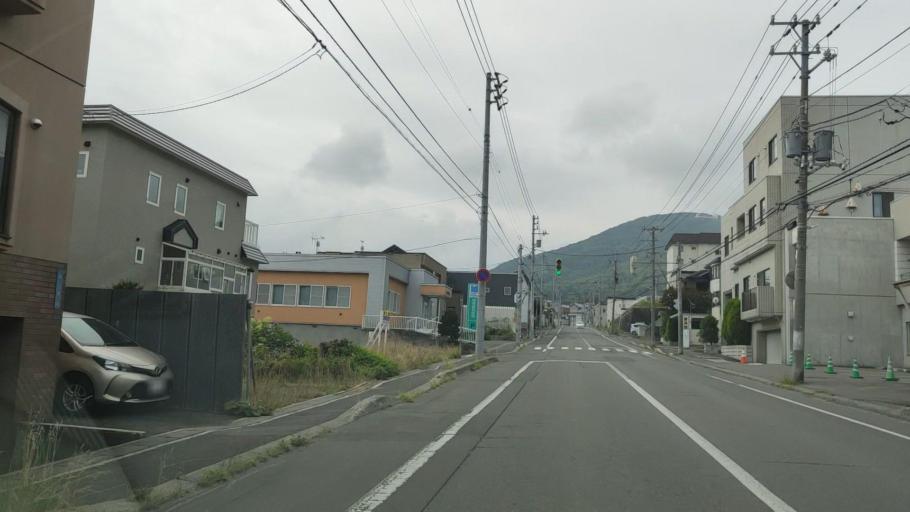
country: JP
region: Hokkaido
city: Otaru
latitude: 43.1869
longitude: 140.9854
